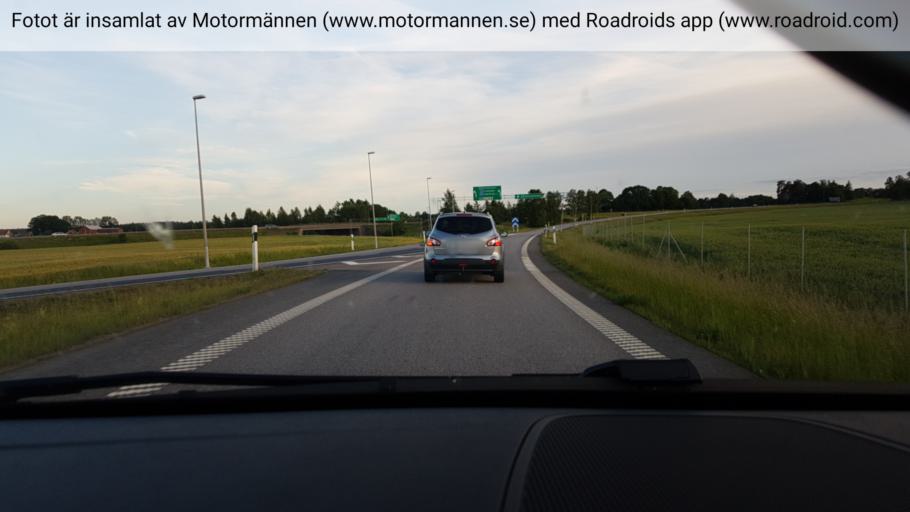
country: SE
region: OEstergoetland
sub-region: Linkopings Kommun
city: Malmslatt
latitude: 58.4369
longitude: 15.5268
